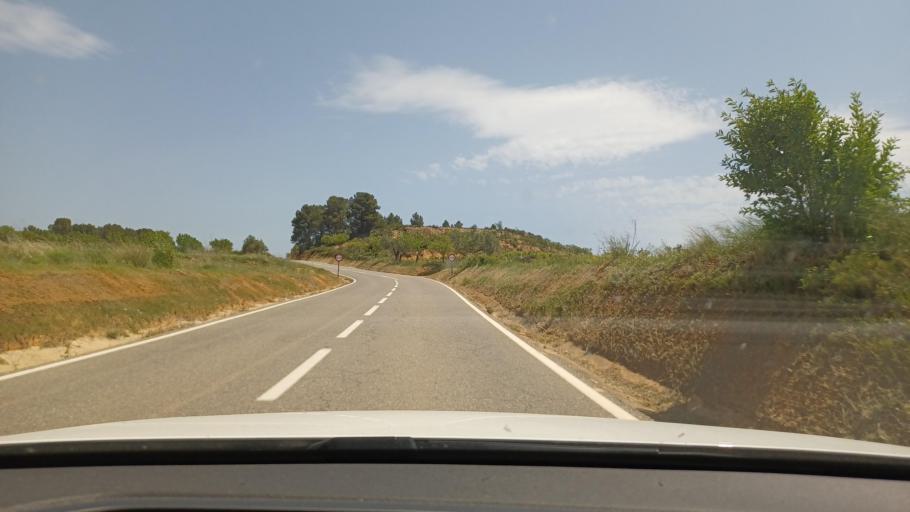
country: ES
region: Catalonia
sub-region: Provincia de Tarragona
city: Gandesa
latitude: 41.0501
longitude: 0.4137
